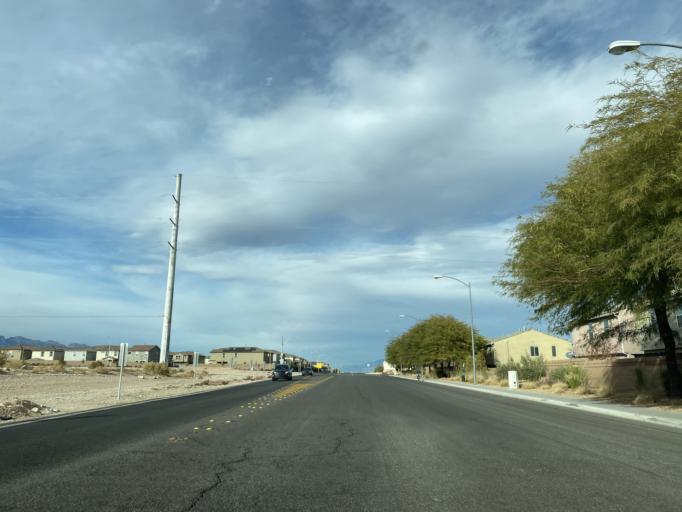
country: US
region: Nevada
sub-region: Clark County
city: Enterprise
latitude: 36.0106
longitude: -115.2982
